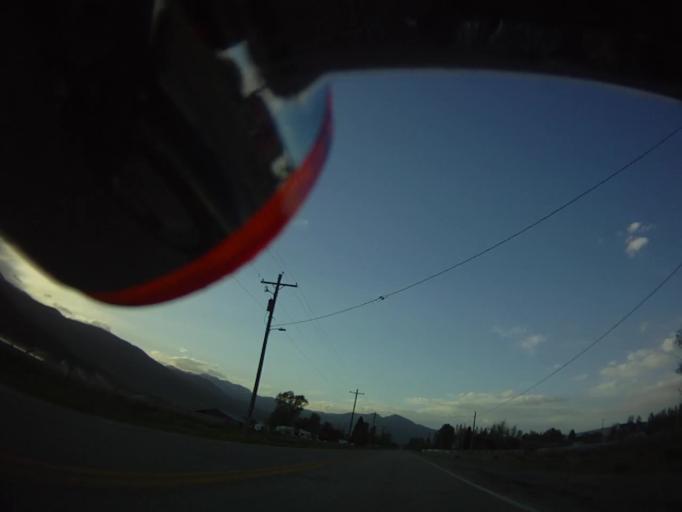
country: US
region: Utah
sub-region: Wasatch County
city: Midway
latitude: 40.4642
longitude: -111.4717
